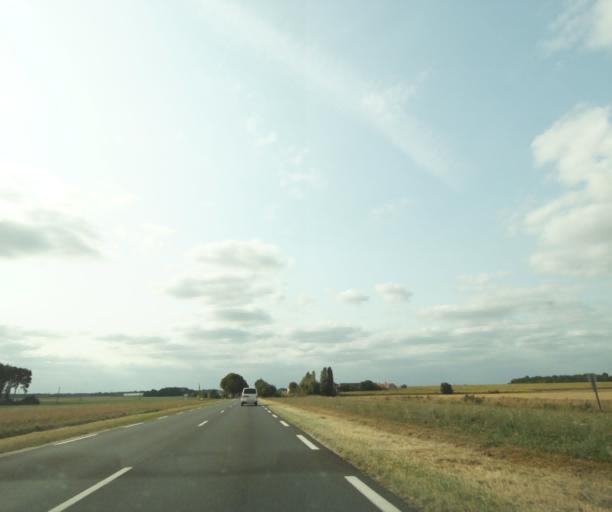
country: FR
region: Centre
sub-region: Departement d'Indre-et-Loire
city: Truyes
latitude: 47.2426
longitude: 0.8605
